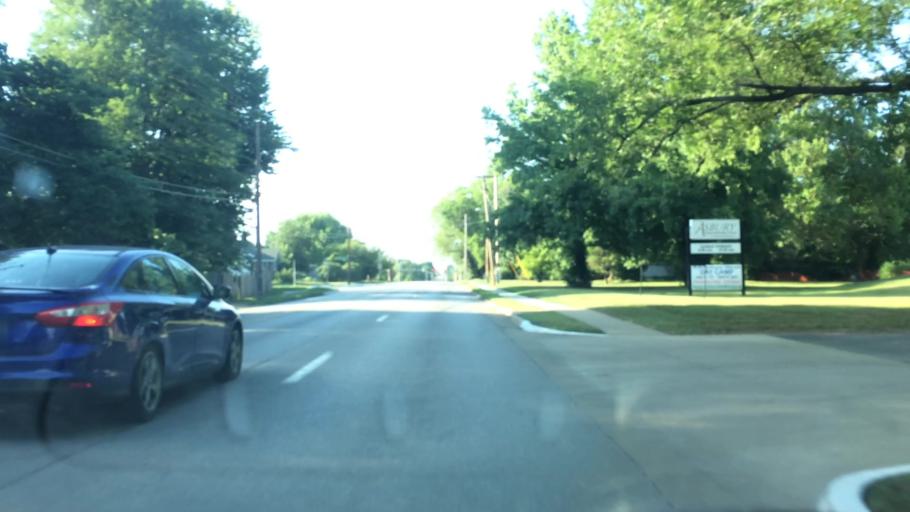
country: US
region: Missouri
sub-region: Greene County
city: Springfield
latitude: 37.1871
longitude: -93.2948
